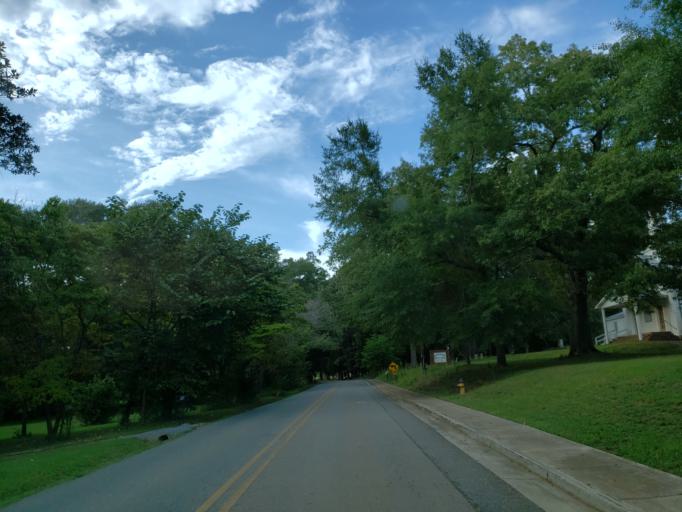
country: US
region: Georgia
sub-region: Bartow County
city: Euharlee
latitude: 34.1457
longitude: -84.9335
